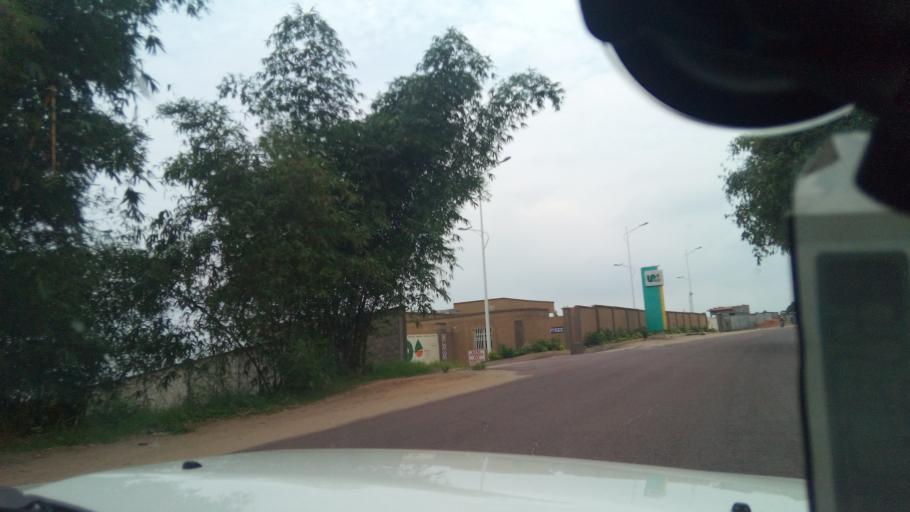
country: CD
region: Kinshasa
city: Masina
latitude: -4.1752
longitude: 15.5437
